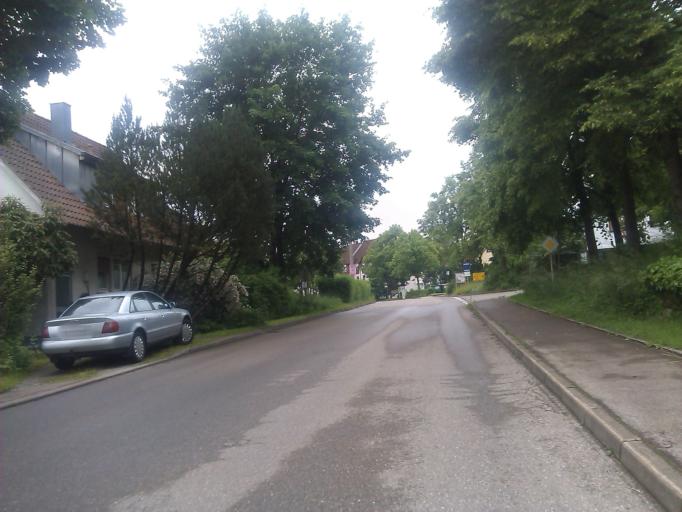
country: DE
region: Baden-Wuerttemberg
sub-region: Regierungsbezirk Stuttgart
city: Oberrot
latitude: 49.0172
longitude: 9.6609
